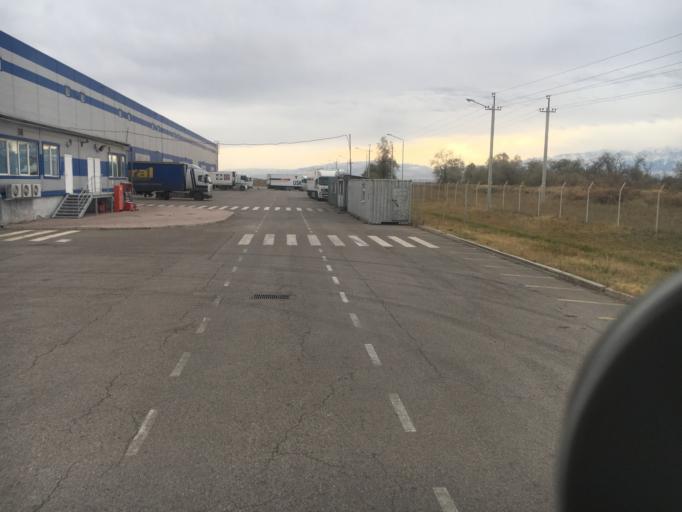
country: KZ
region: Almaty Oblysy
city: Energeticheskiy
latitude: 43.5833
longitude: 77.0945
